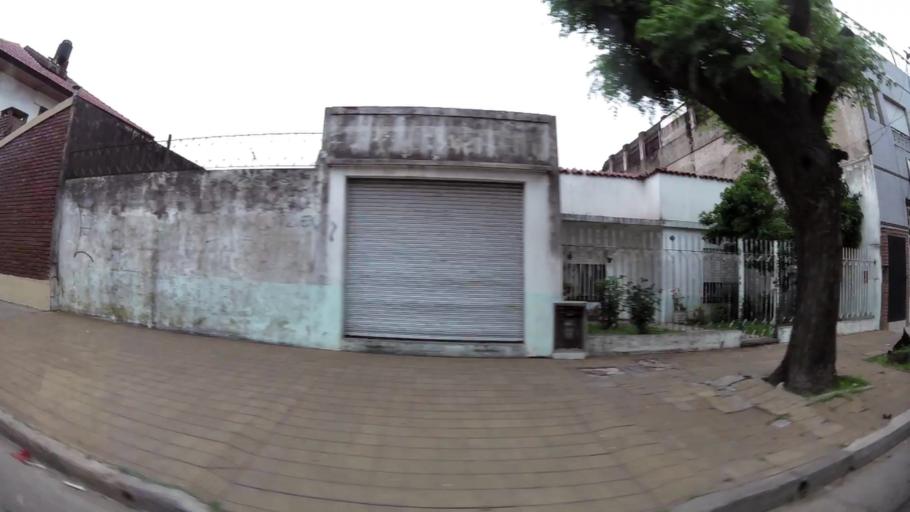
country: AR
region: Buenos Aires F.D.
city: Villa Lugano
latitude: -34.7105
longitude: -58.5168
